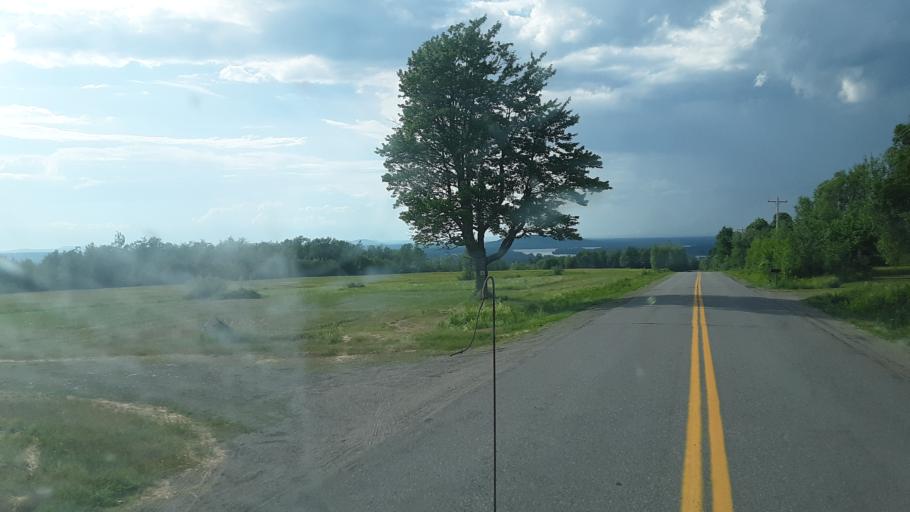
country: US
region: Maine
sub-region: Washington County
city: Calais
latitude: 45.0942
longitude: -67.5071
